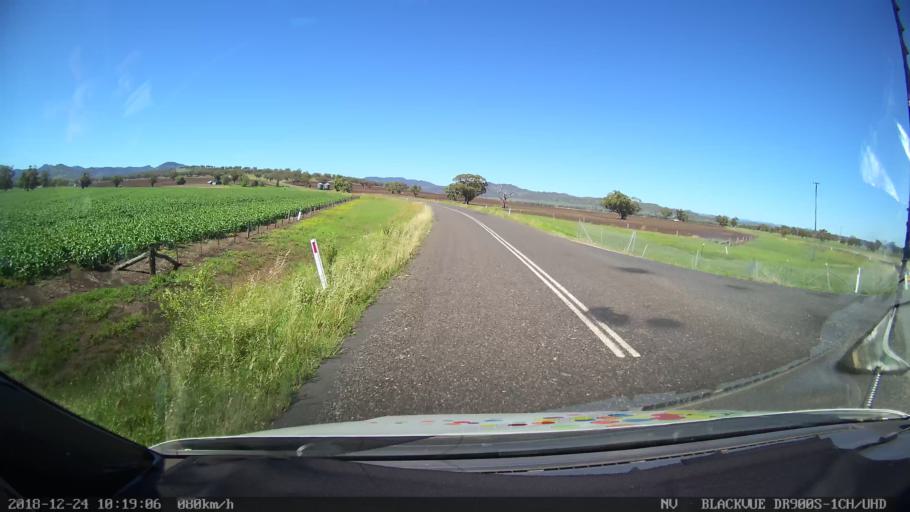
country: AU
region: New South Wales
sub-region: Liverpool Plains
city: Quirindi
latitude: -31.7267
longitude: 150.5670
